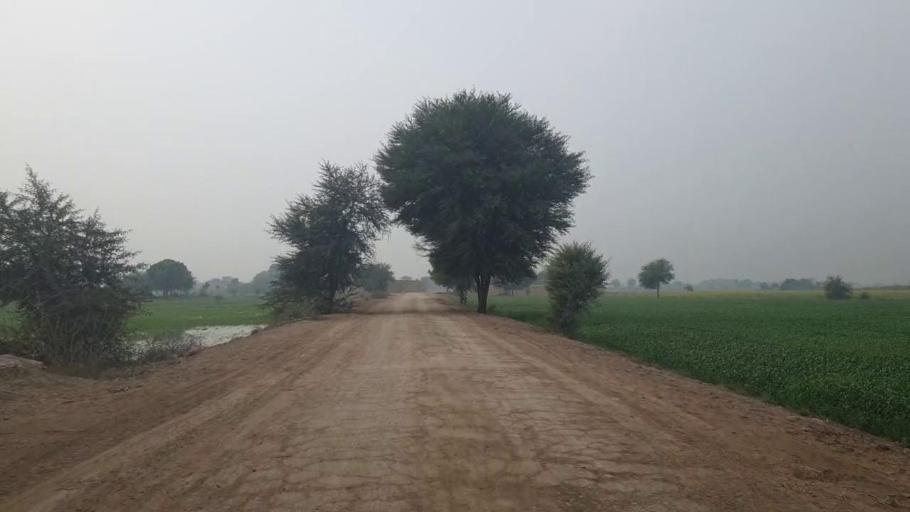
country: PK
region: Sindh
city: Tando Adam
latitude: 25.7137
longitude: 68.6183
